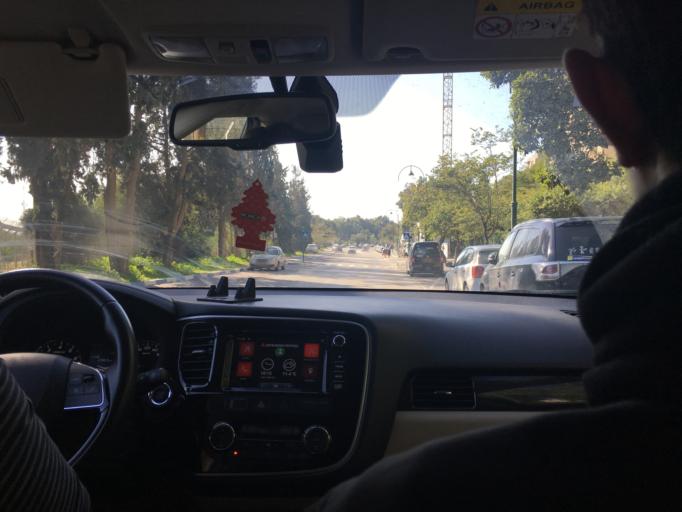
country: IL
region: Tel Aviv
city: Ramat HaSharon
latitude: 32.1429
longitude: 34.8469
